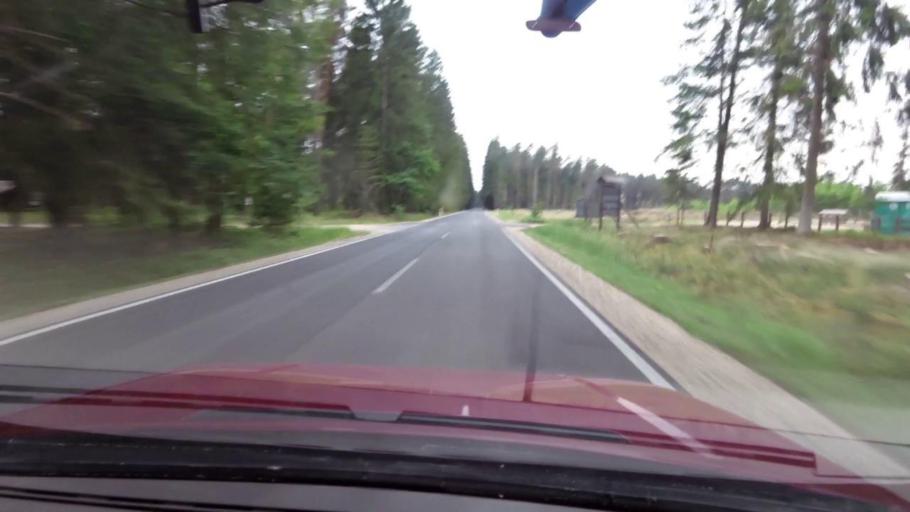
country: PL
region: West Pomeranian Voivodeship
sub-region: Powiat koszalinski
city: Polanow
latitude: 54.1430
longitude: 16.4857
